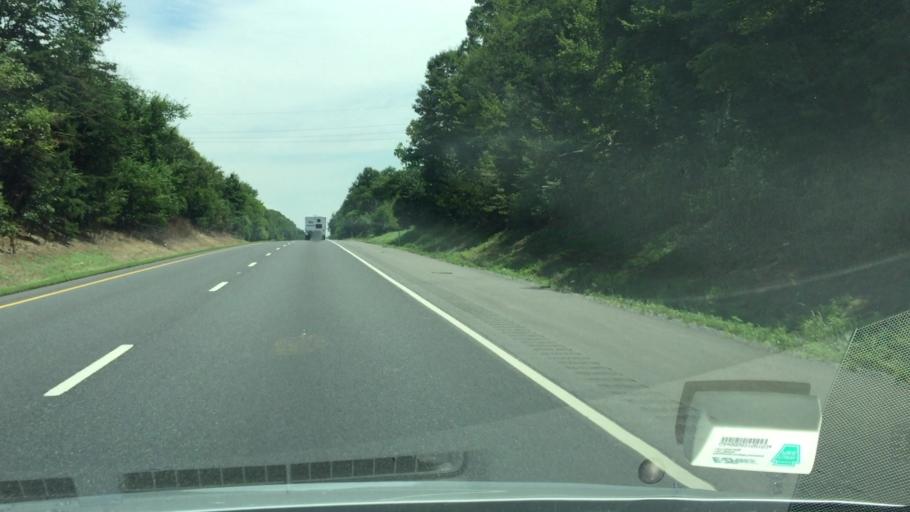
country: US
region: Maryland
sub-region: Washington County
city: Wilson-Conococheague
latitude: 39.6257
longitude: -77.9909
